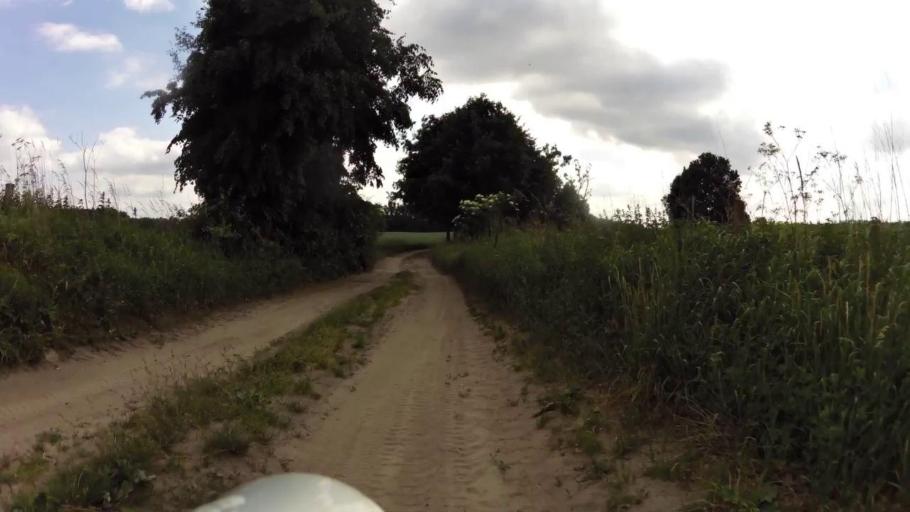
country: PL
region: West Pomeranian Voivodeship
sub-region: Powiat koszalinski
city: Bobolice
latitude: 53.9599
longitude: 16.6852
